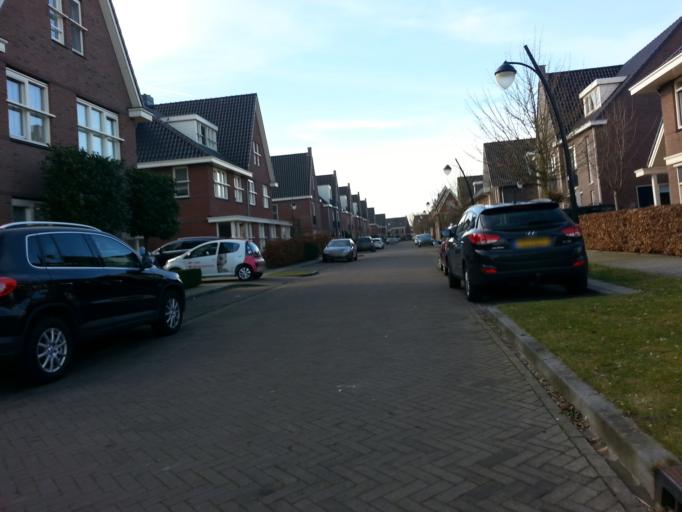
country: NL
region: Utrecht
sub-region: Gemeente Leusden
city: Leusden
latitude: 52.1199
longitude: 5.4132
